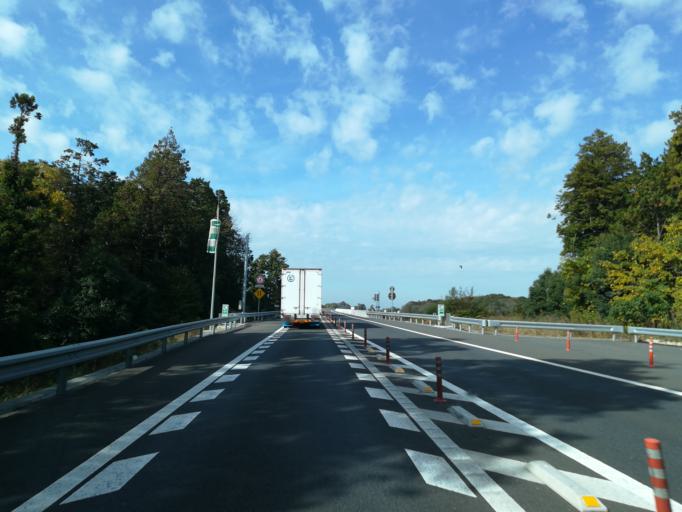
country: JP
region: Ibaraki
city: Mitsukaido
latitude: 36.0677
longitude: 140.0223
